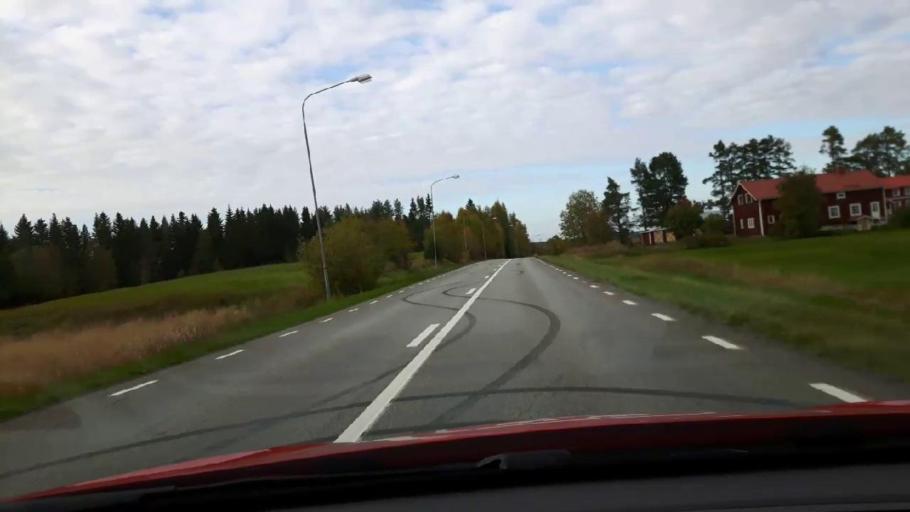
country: SE
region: Jaemtland
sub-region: Krokoms Kommun
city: Valla
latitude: 63.2388
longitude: 14.0041
